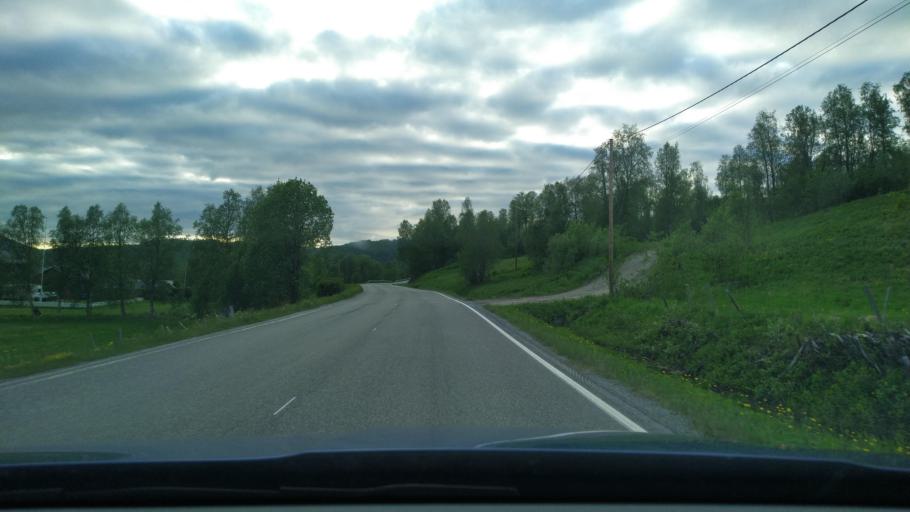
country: NO
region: Troms
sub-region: Sorreisa
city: Sorreisa
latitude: 69.0888
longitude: 18.3514
